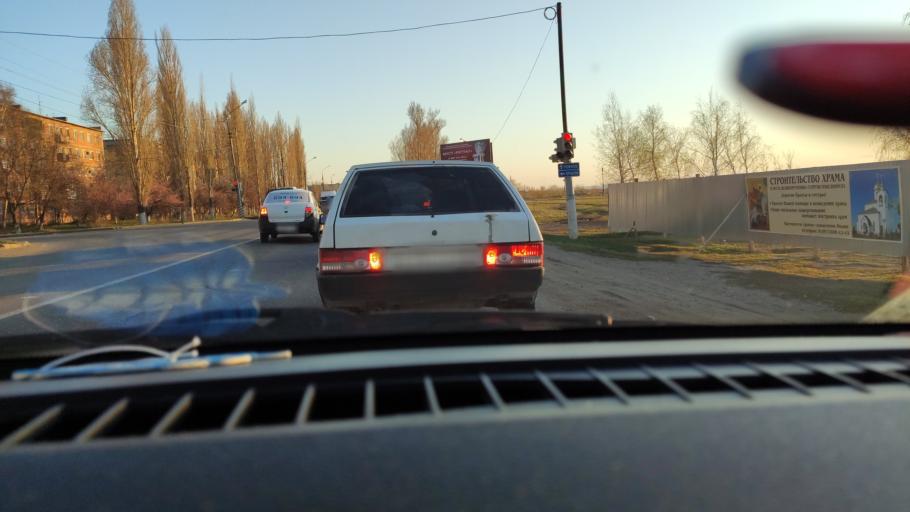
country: RU
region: Saratov
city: Engel's
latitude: 51.4523
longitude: 46.0836
